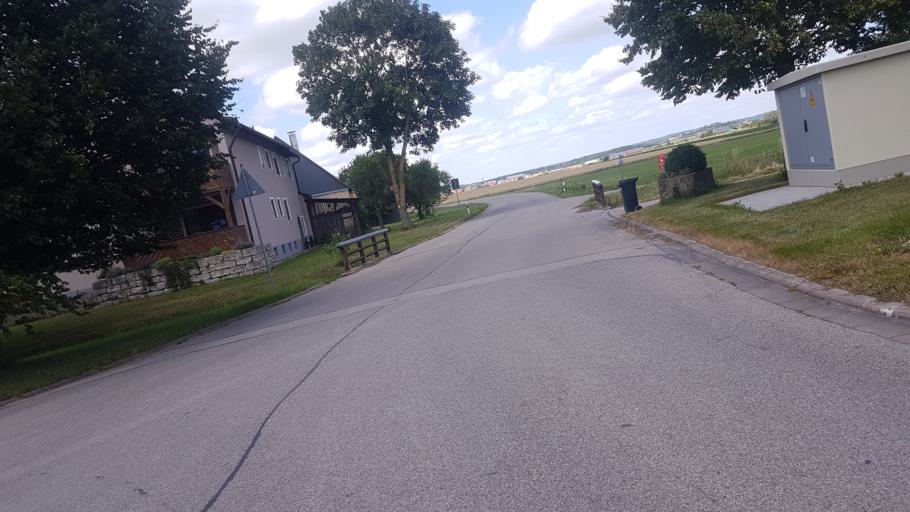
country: DE
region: Bavaria
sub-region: Regierungsbezirk Mittelfranken
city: Geslau
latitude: 49.3473
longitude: 10.3283
